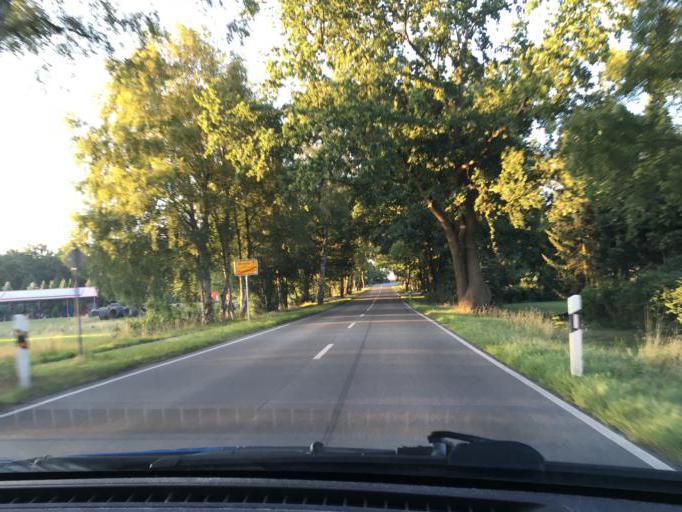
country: DE
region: Lower Saxony
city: Wriedel
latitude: 53.0208
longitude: 10.2805
